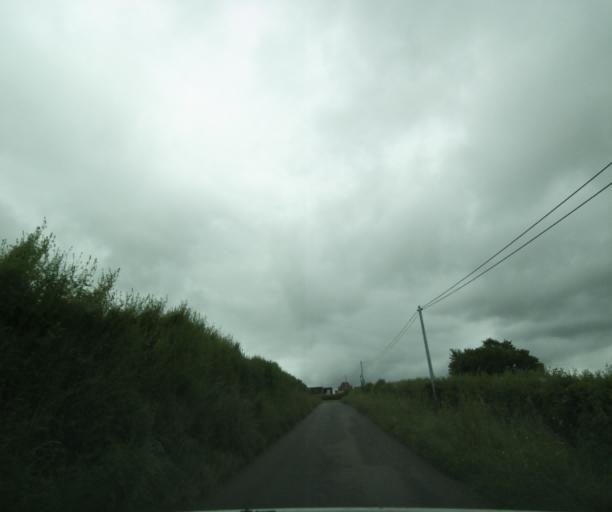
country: FR
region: Bourgogne
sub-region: Departement de Saone-et-Loire
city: Charolles
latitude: 46.4787
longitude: 4.3233
